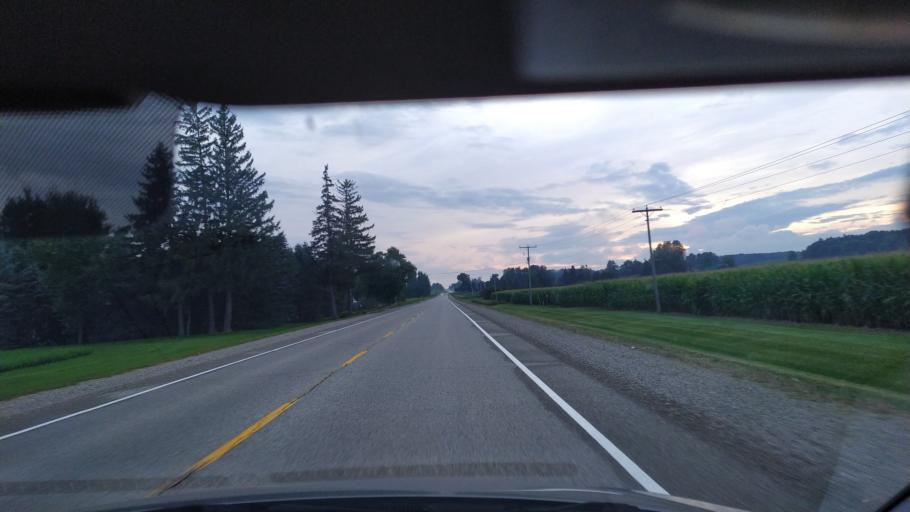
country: CA
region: Ontario
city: Kitchener
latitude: 43.3148
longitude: -80.5483
